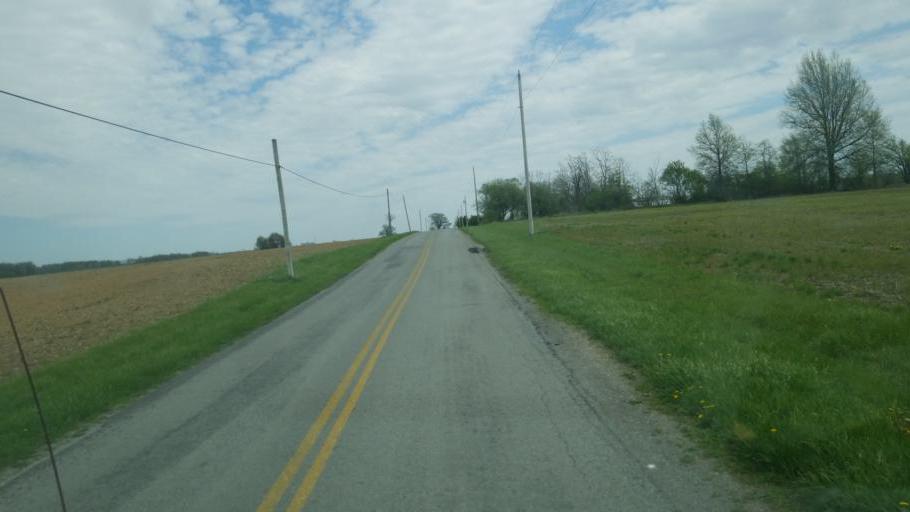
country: US
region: Ohio
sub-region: Hardin County
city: Ada
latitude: 40.8198
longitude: -83.8318
